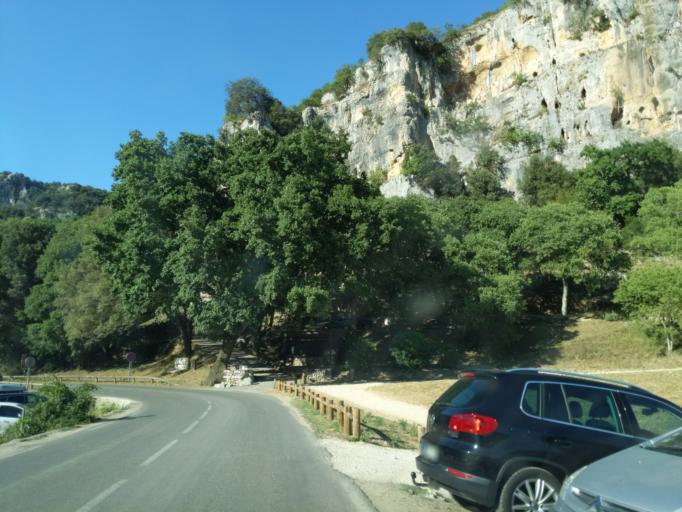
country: FR
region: Languedoc-Roussillon
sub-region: Departement du Gard
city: Barjac
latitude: 44.3839
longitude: 4.4140
